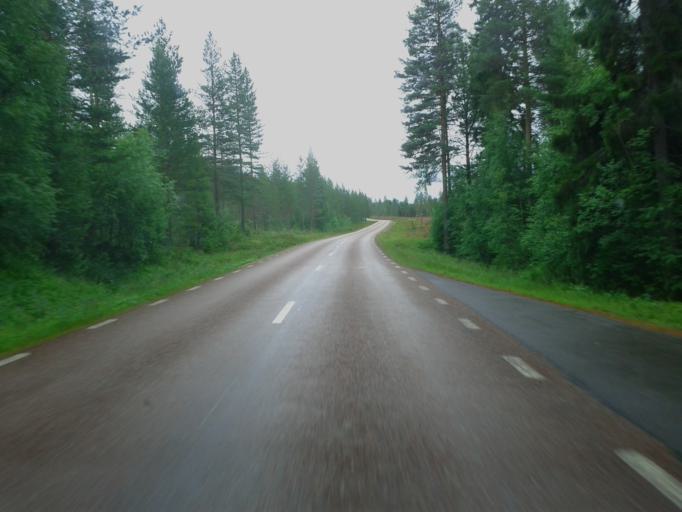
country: NO
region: Hedmark
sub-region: Trysil
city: Innbygda
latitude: 61.7807
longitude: 12.9402
